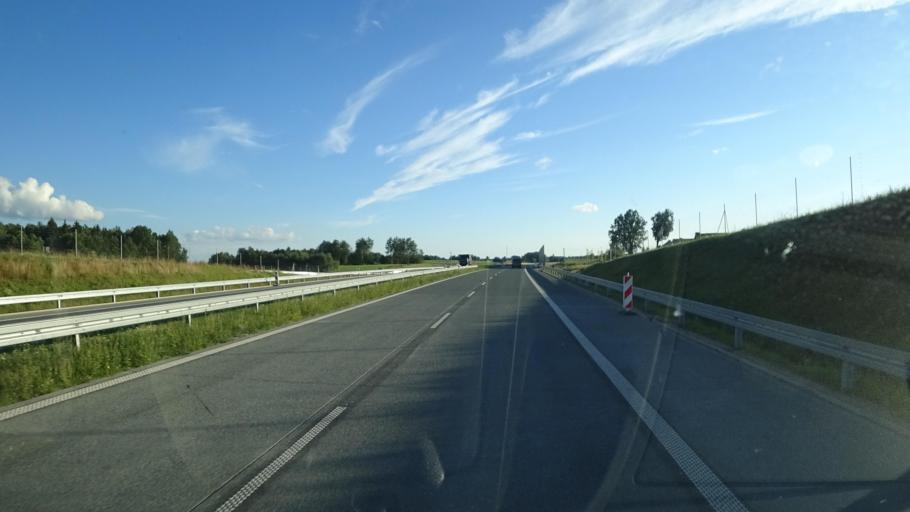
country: PL
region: Podlasie
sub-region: Powiat suwalski
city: Raczki
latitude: 53.9243
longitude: 22.7494
